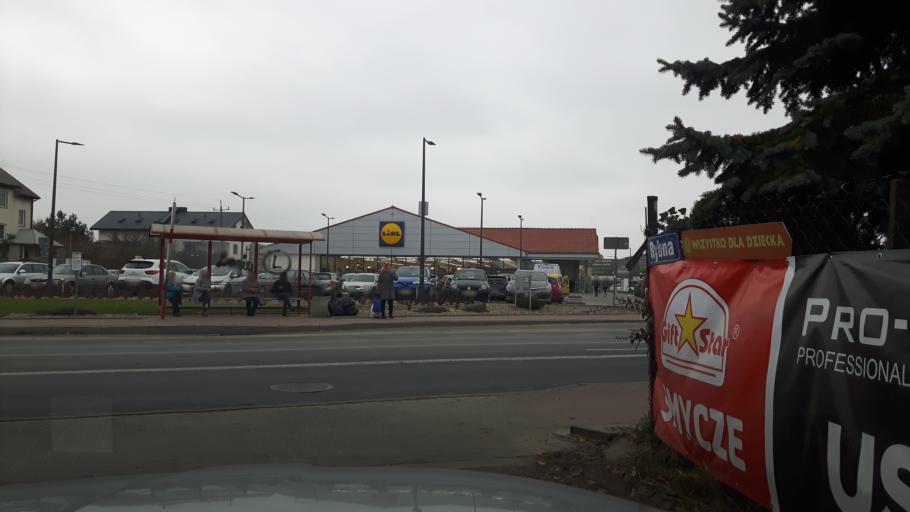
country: PL
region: Masovian Voivodeship
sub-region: Powiat wolominski
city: Zabki
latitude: 52.2821
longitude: 21.1113
